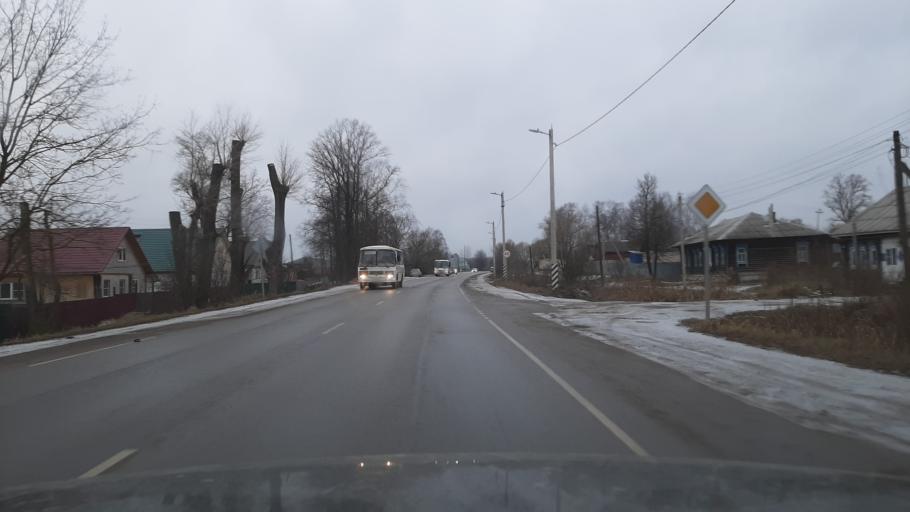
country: RU
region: Ivanovo
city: Kitovo
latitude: 56.8639
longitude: 41.2937
